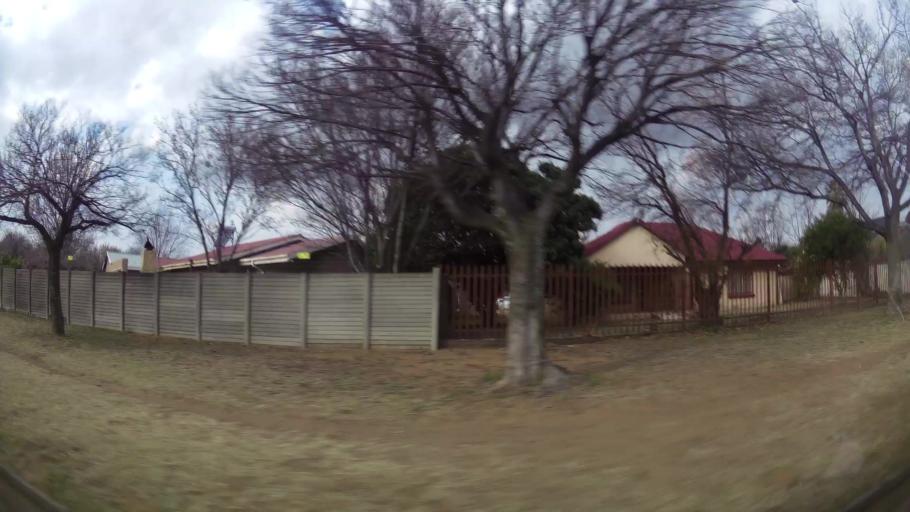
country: ZA
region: Orange Free State
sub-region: Fezile Dabi District Municipality
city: Sasolburg
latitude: -26.8149
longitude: 27.8300
